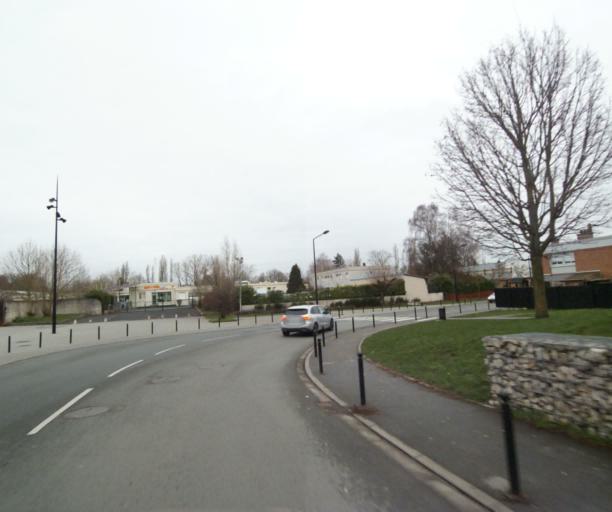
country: FR
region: Nord-Pas-de-Calais
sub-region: Departement du Nord
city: La Sentinelle
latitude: 50.3541
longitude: 3.4900
